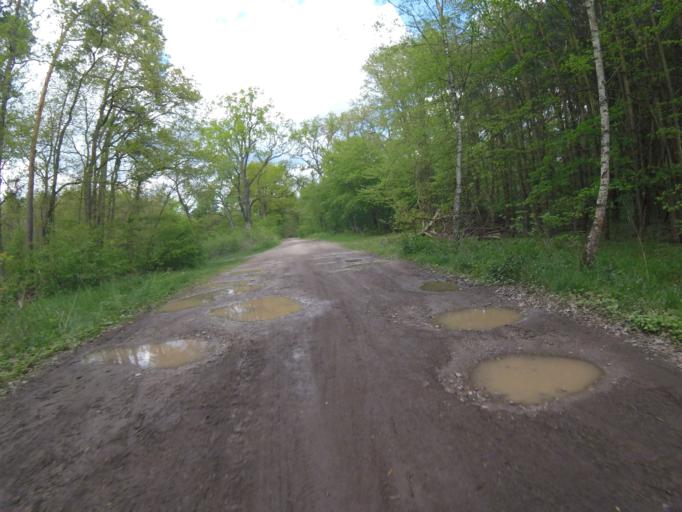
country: DE
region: Brandenburg
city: Schwerin
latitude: 52.1723
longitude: 13.5954
